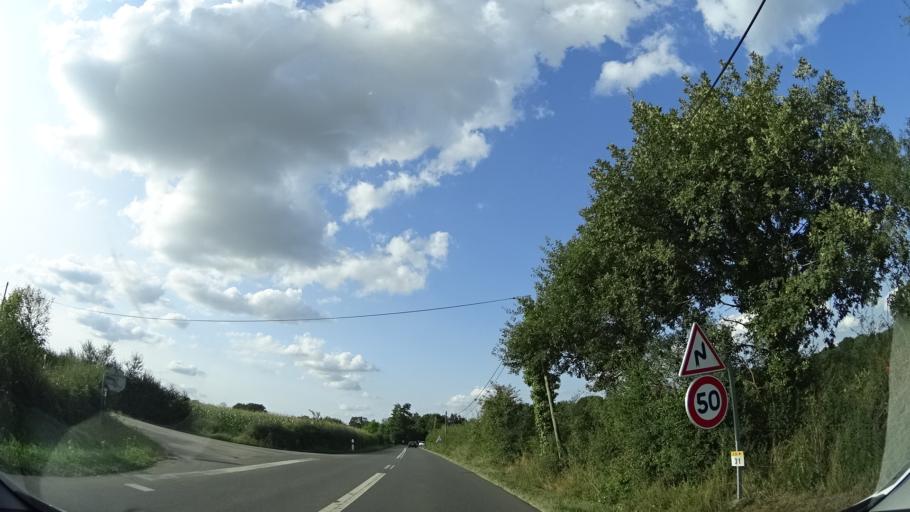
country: FR
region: Pays de la Loire
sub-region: Departement de la Loire-Atlantique
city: Casson
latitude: 47.4085
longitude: -1.5352
